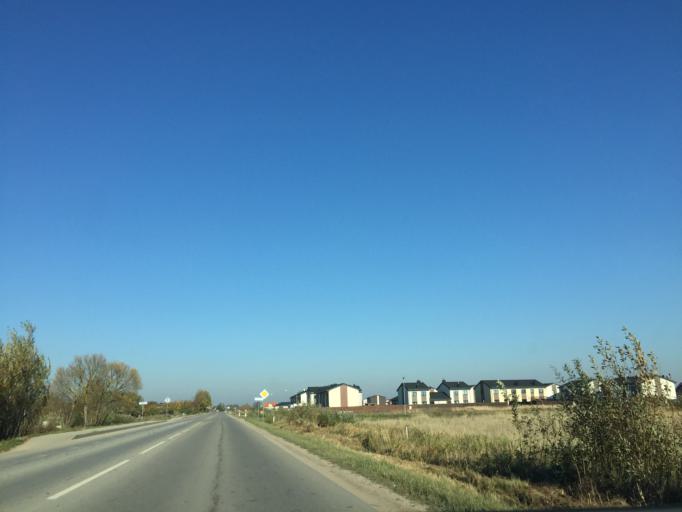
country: LT
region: Klaipedos apskritis
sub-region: Klaipeda
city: Klaipeda
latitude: 55.7387
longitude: 21.1927
